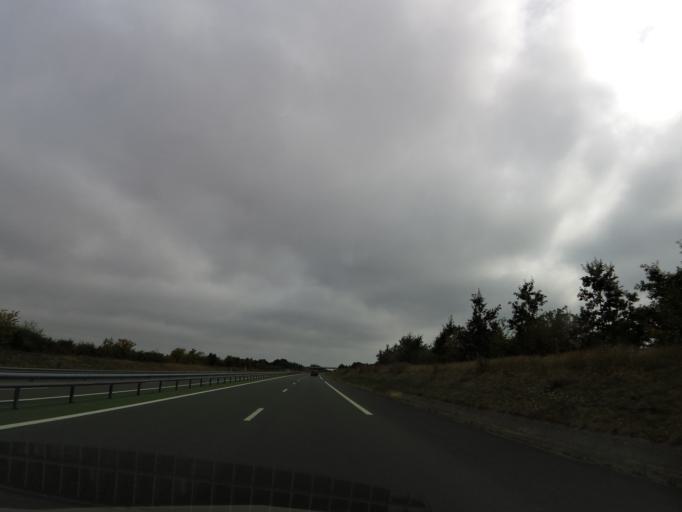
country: FR
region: Pays de la Loire
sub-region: Departement de la Vendee
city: La Ferriere
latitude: 46.6863
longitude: -1.3253
